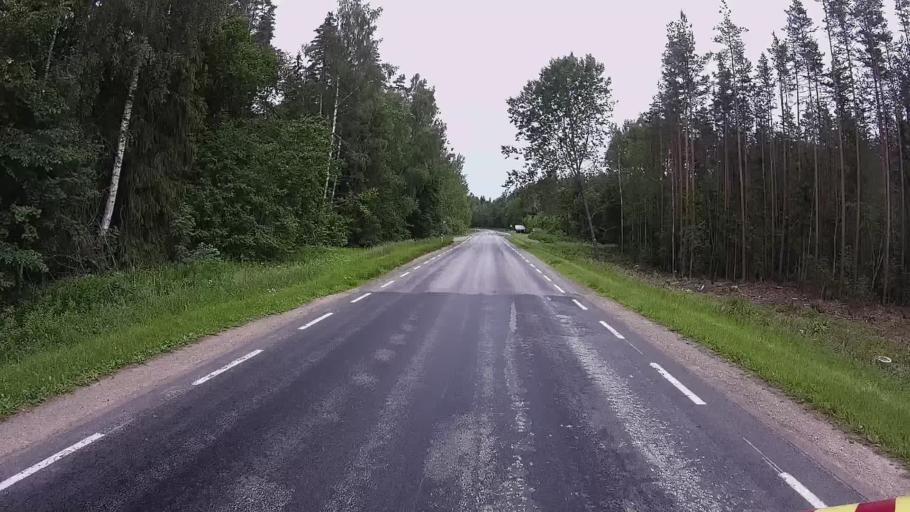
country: EE
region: Viljandimaa
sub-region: Karksi vald
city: Karksi-Nuia
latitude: 58.2072
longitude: 25.6210
